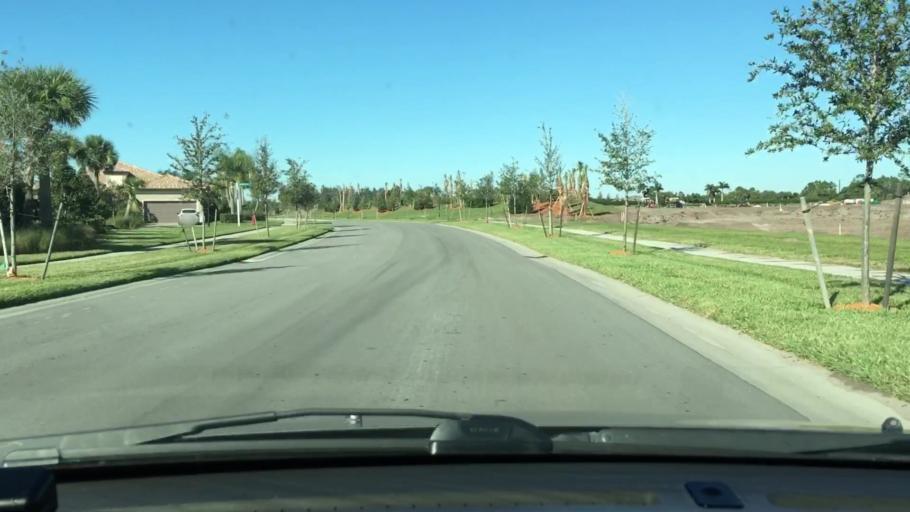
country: US
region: Florida
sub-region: Indian River County
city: Gifford
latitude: 27.6894
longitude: -80.4317
